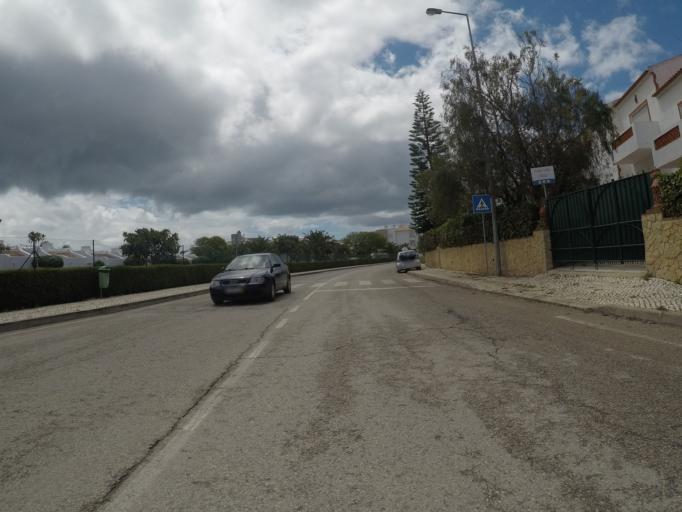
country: PT
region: Faro
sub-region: Lagos
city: Lagos
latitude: 37.0908
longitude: -8.6766
